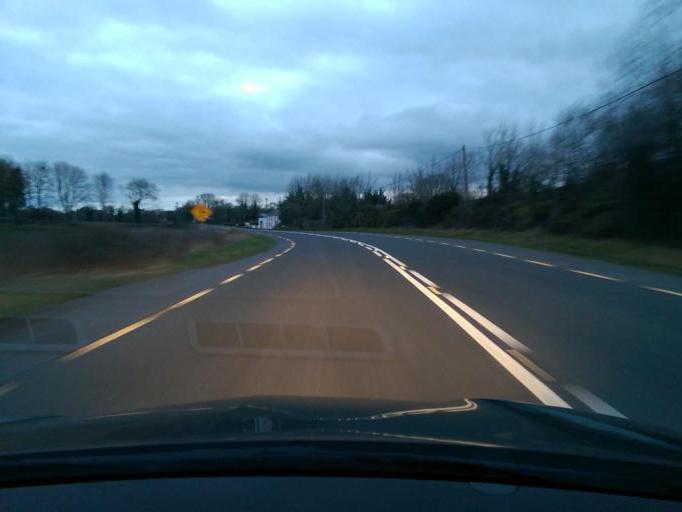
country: IE
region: Connaught
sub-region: County Galway
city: Portumna
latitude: 53.1774
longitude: -8.3391
